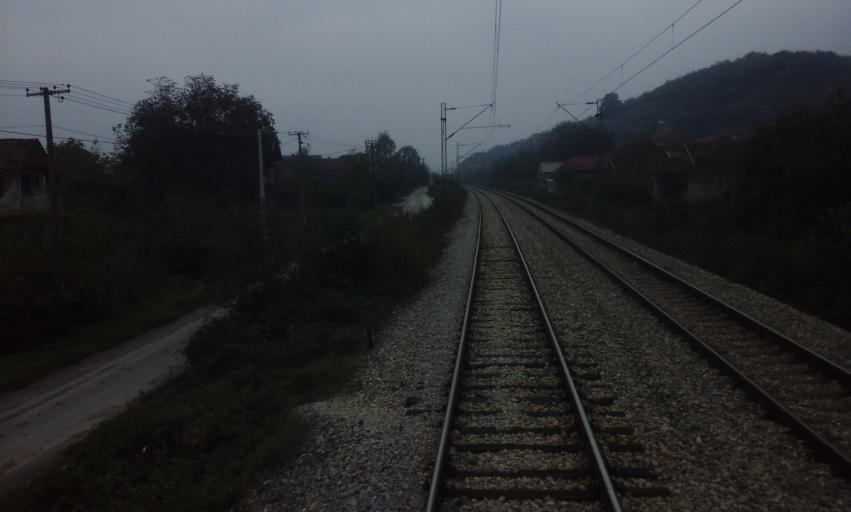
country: RS
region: Central Serbia
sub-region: Pomoravski Okrug
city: Jagodina
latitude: 44.0076
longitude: 21.2323
